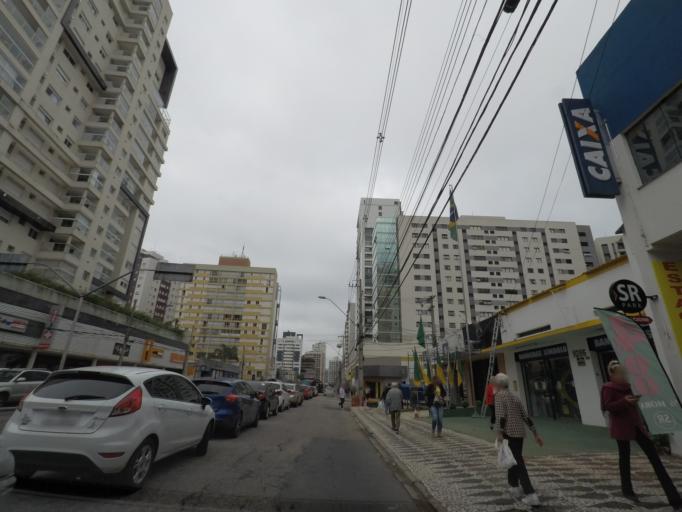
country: BR
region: Parana
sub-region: Curitiba
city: Curitiba
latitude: -25.4561
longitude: -49.2885
